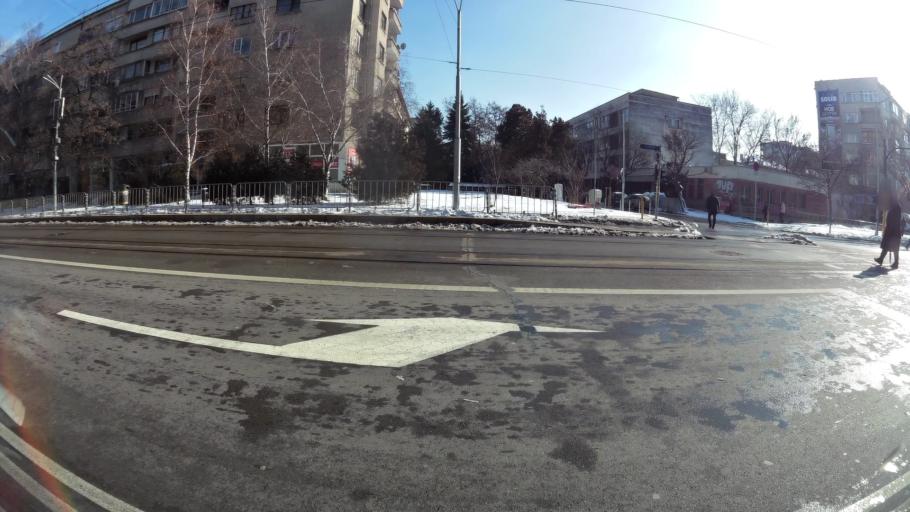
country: BG
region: Sofia-Capital
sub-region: Stolichna Obshtina
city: Sofia
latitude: 42.6795
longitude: 23.3109
